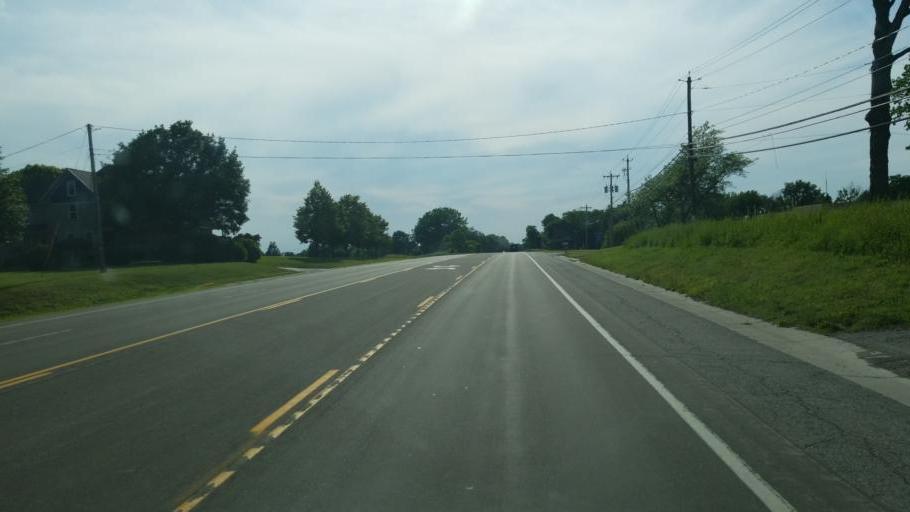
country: US
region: New York
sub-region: Genesee County
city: Batavia
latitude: 42.9875
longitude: -78.1209
